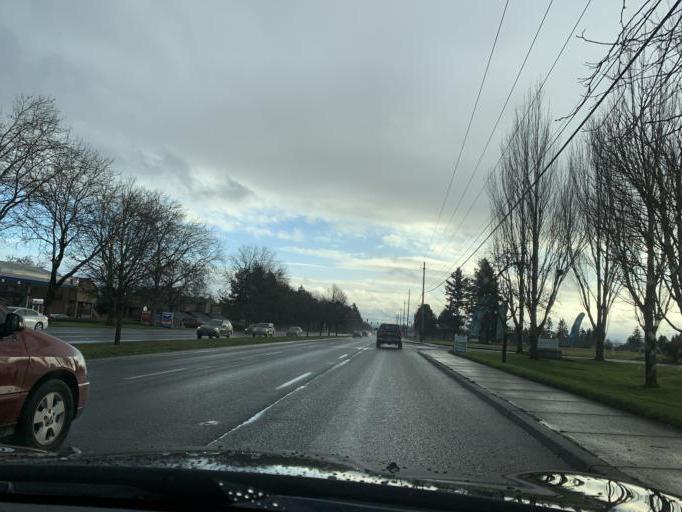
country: US
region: Washington
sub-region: Clark County
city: Mill Plain
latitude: 45.6025
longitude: -122.5040
